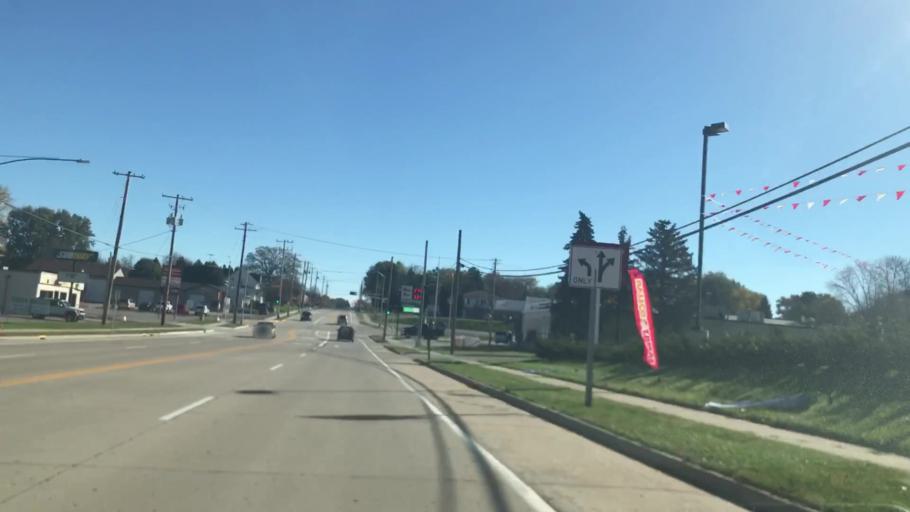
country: US
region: Wisconsin
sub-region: Dodge County
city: Mayville
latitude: 43.4940
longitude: -88.5580
